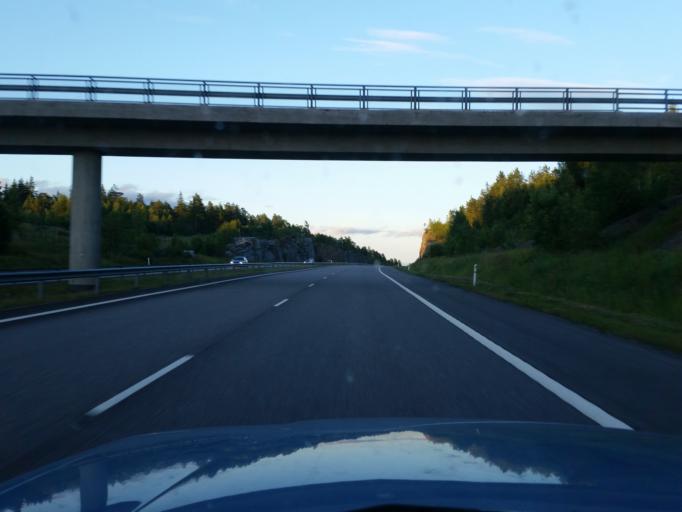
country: FI
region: Varsinais-Suomi
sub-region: Salo
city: Halikko
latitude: 60.4350
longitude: 22.9559
